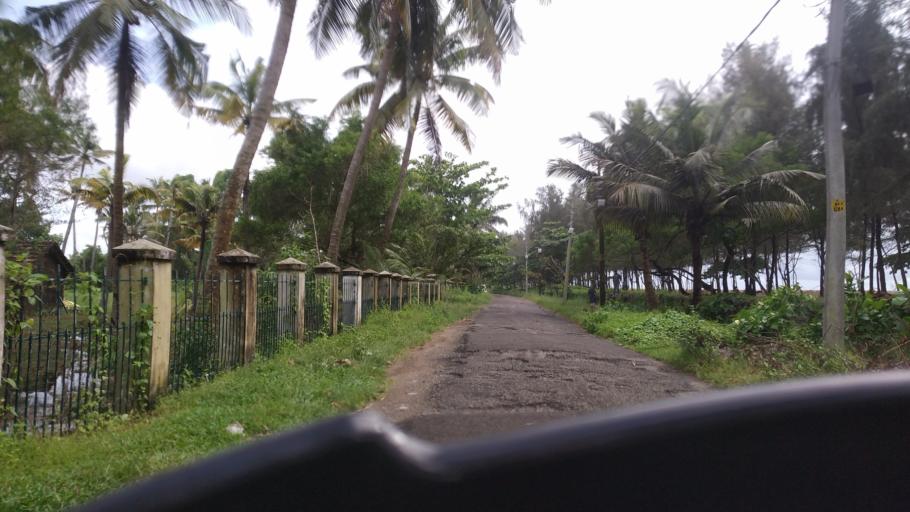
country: IN
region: Kerala
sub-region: Ernakulam
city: Elur
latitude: 10.1079
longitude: 76.1881
